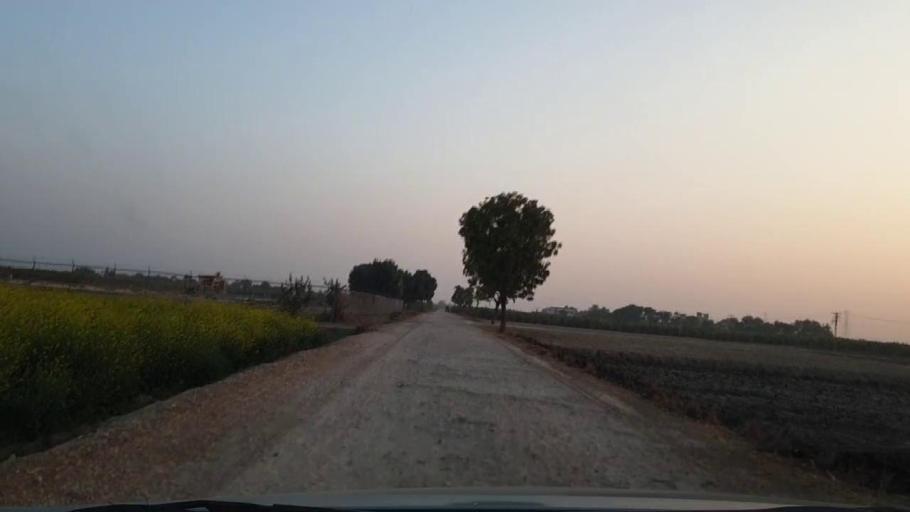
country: PK
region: Sindh
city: Matiari
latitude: 25.6827
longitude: 68.5240
